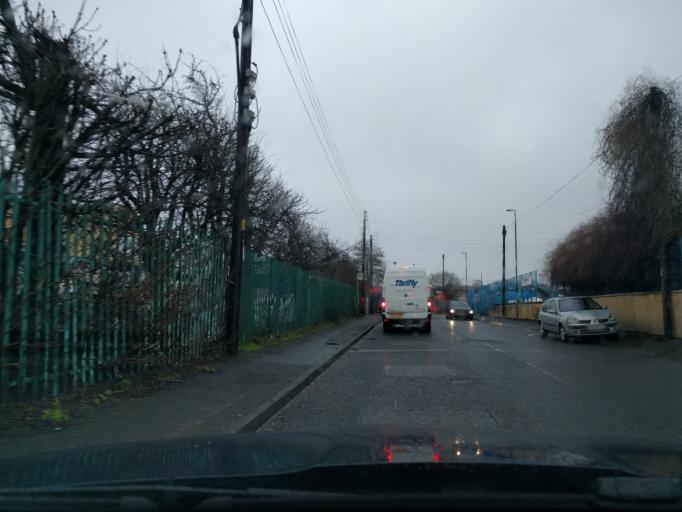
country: GB
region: England
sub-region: Gateshead
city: Felling
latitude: 54.9551
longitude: -1.5613
